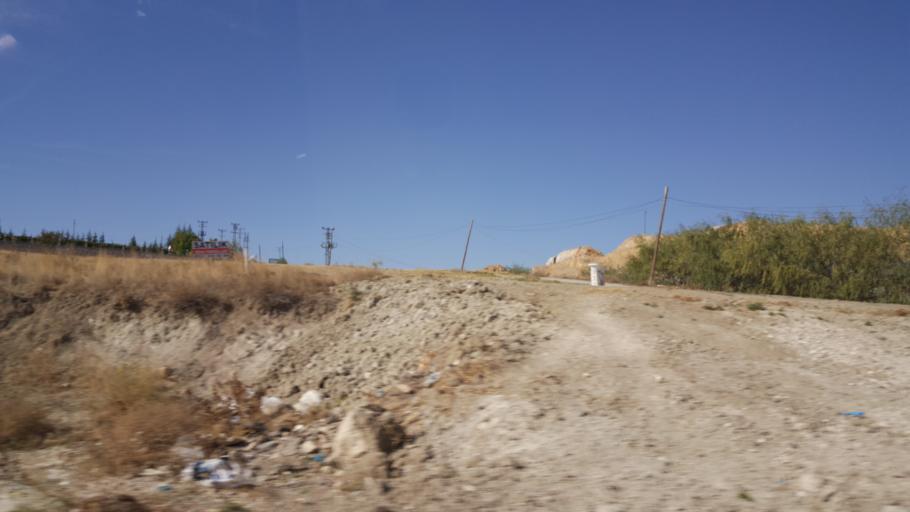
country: TR
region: Ankara
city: Ikizce
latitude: 39.6577
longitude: 32.7270
